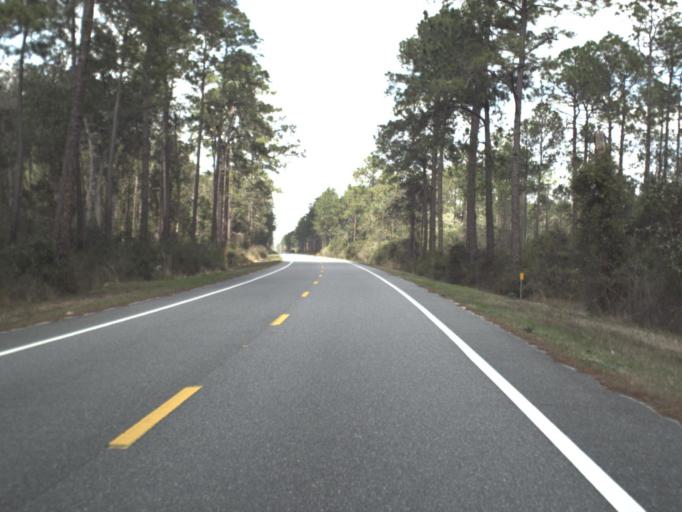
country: US
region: Florida
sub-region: Franklin County
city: Apalachicola
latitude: 29.9749
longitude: -84.9749
